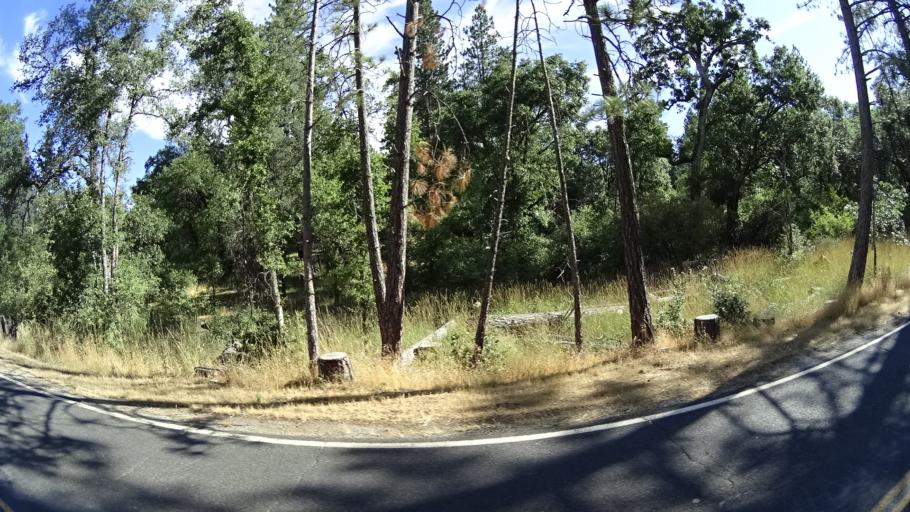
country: US
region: California
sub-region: Amador County
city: Pioneer
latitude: 38.3742
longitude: -120.4718
